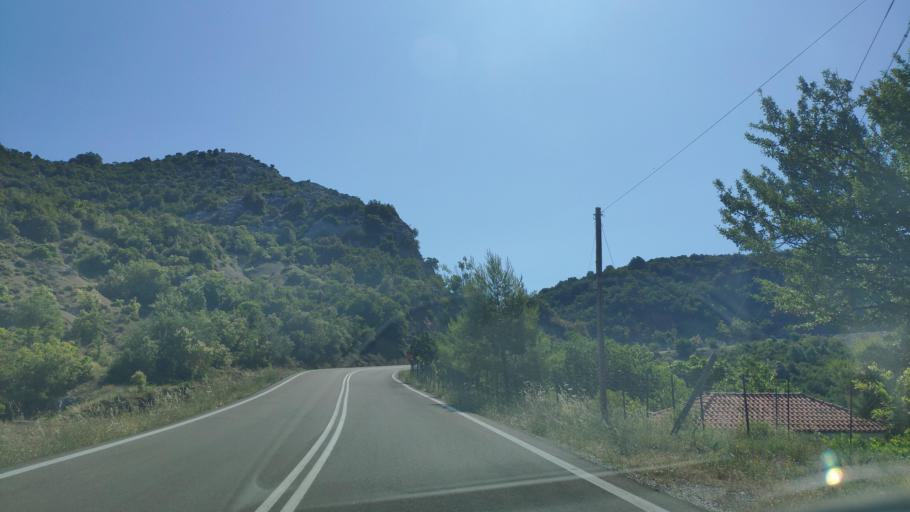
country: GR
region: West Greece
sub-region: Nomos Aitolias kai Akarnanias
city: Sardinia
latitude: 38.9249
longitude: 21.4171
